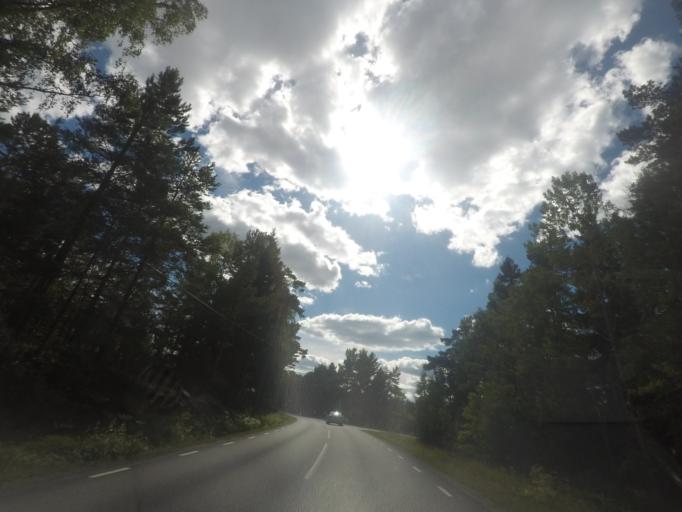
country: SE
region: Stockholm
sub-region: Norrtalje Kommun
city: Arno
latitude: 60.0934
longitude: 18.7954
